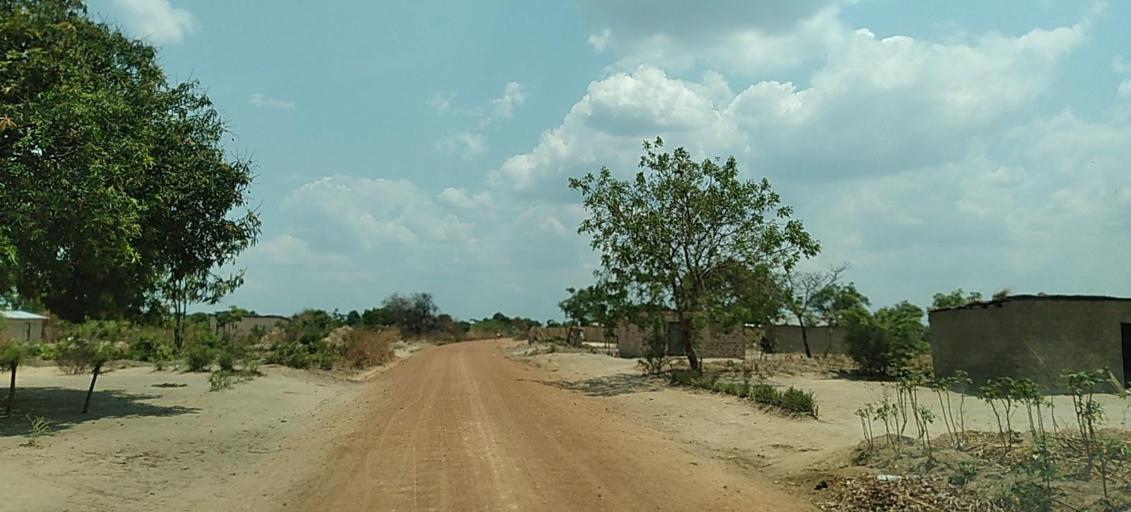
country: ZM
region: Copperbelt
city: Luanshya
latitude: -13.1322
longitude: 28.3133
